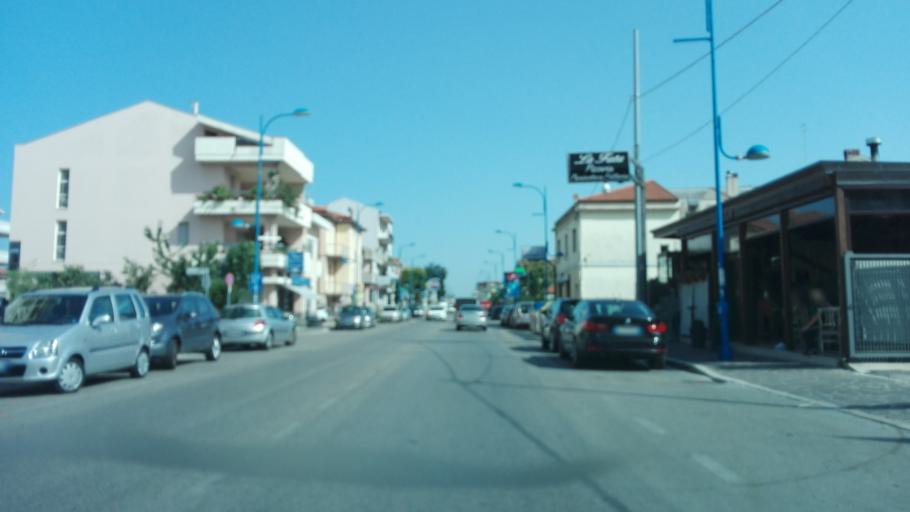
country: IT
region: Abruzzo
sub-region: Provincia di Pescara
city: Montesilvano Marina
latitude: 42.5021
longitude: 14.1674
